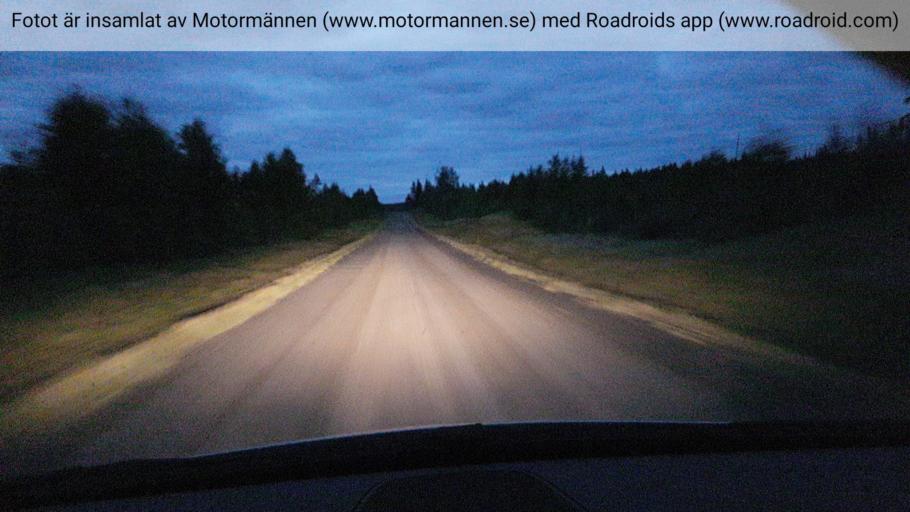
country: SE
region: Jaemtland
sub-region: Braecke Kommun
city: Braecke
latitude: 63.2544
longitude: 15.3709
